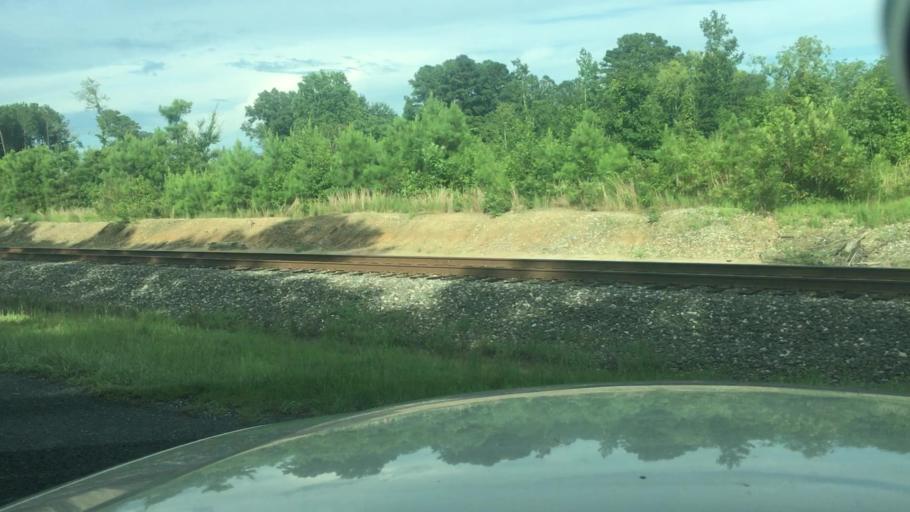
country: US
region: North Carolina
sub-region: Cumberland County
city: Eastover
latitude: 35.1548
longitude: -78.8541
